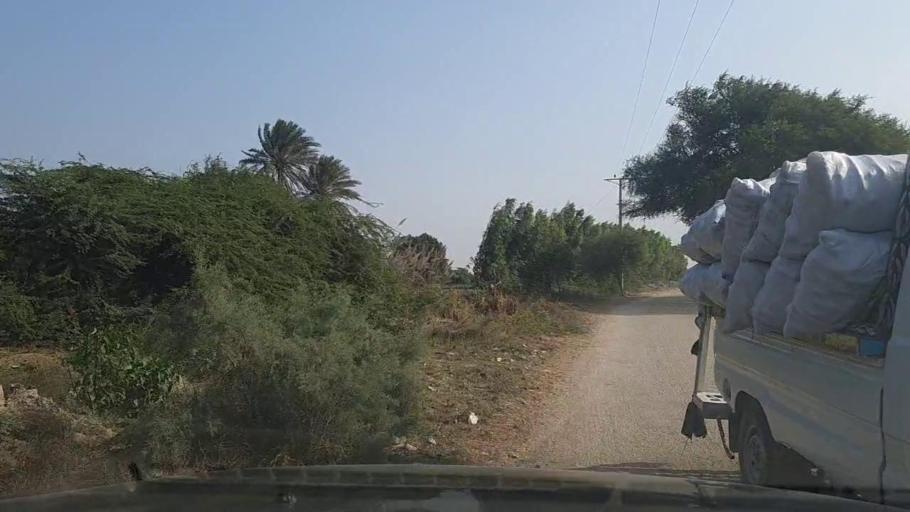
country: PK
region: Sindh
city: Mirpur Sakro
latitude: 24.6332
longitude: 67.7561
